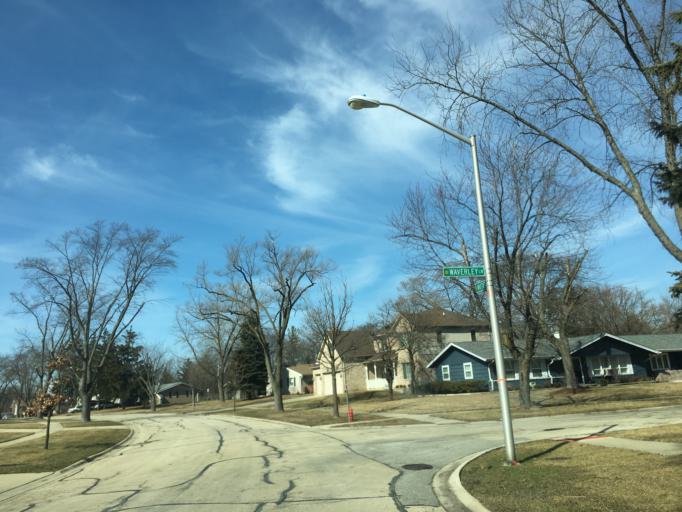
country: US
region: Illinois
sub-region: DuPage County
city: Hanover Park
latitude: 42.0200
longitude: -88.1264
